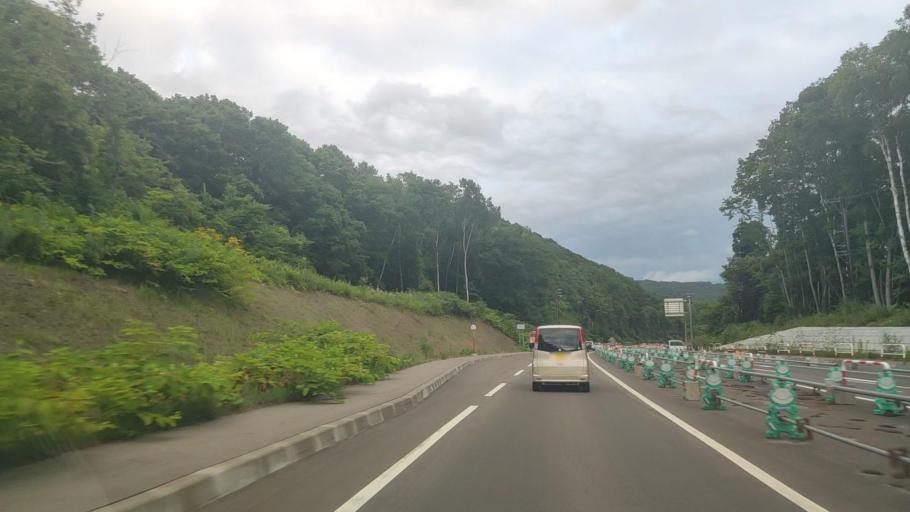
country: JP
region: Hokkaido
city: Nanae
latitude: 41.9884
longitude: 140.6391
